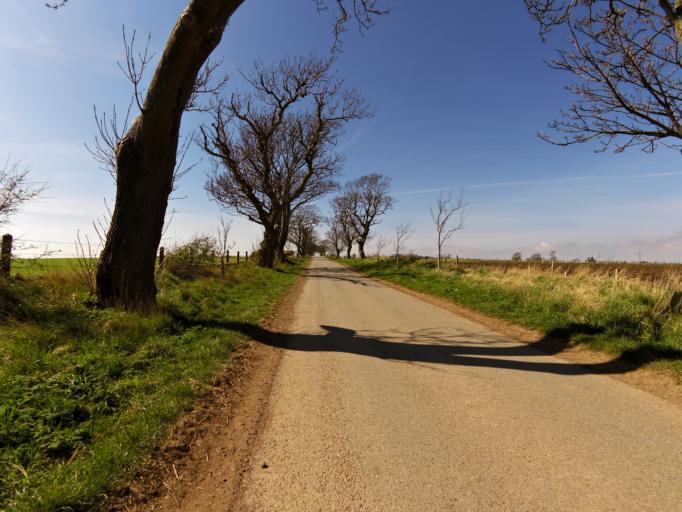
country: GB
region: Scotland
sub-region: Angus
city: Montrose
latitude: 56.6839
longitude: -2.4583
